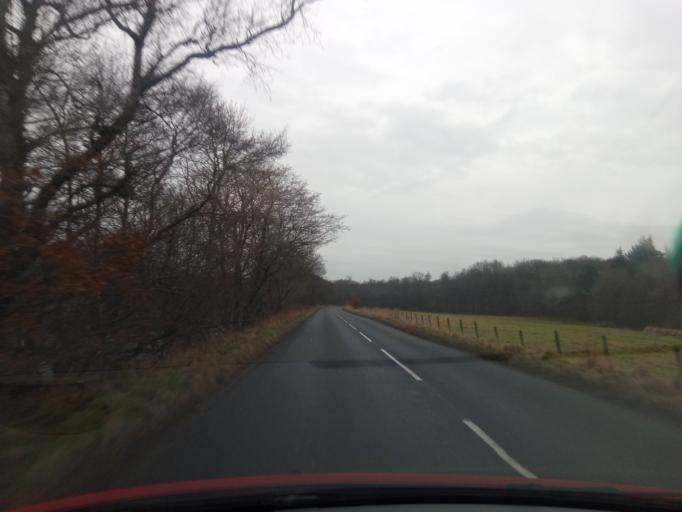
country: GB
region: England
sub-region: Northumberland
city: Rochester
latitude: 55.1657
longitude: -2.4164
